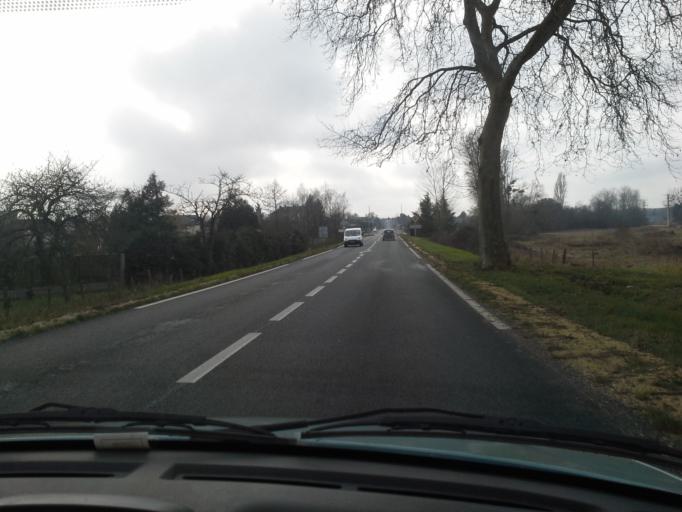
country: FR
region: Centre
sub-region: Departement d'Indre-et-Loire
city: Monnaie
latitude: 47.5072
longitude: 0.7986
